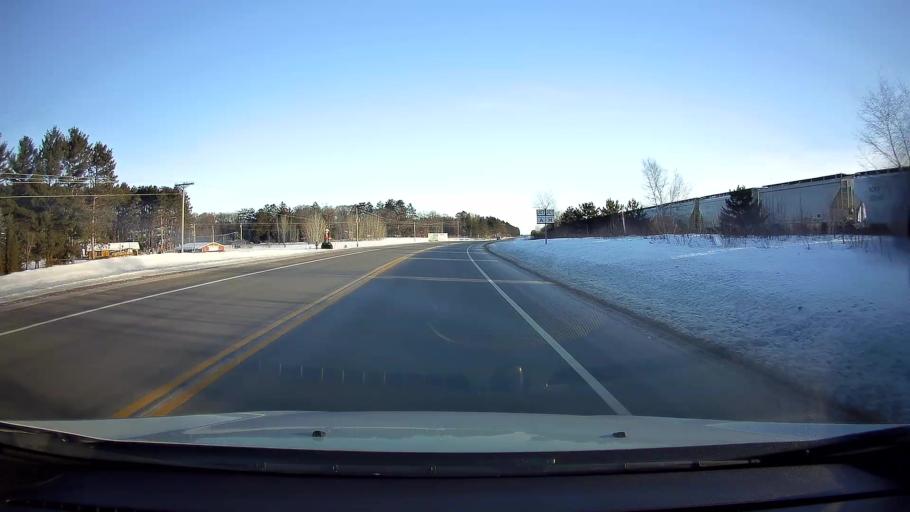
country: US
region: Wisconsin
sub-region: Washburn County
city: Spooner
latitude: 45.8410
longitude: -91.8784
